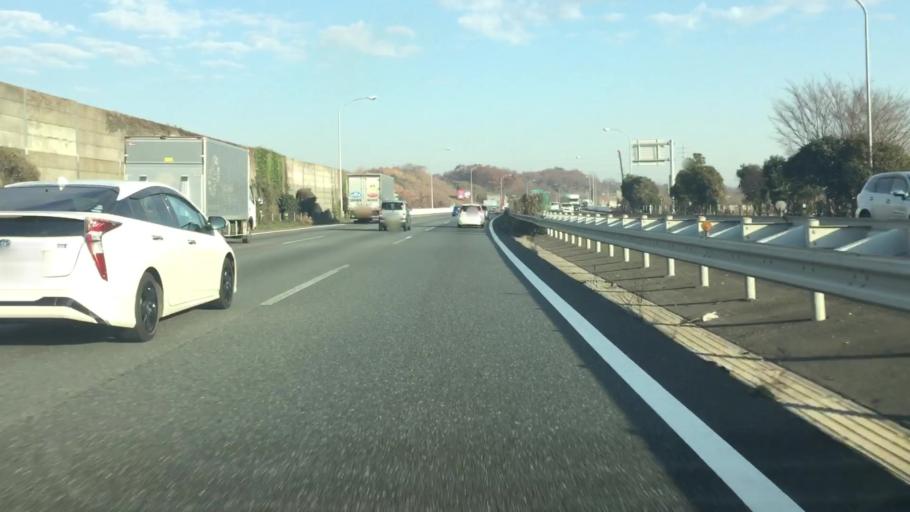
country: JP
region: Saitama
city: Sakado
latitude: 35.9786
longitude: 139.3799
